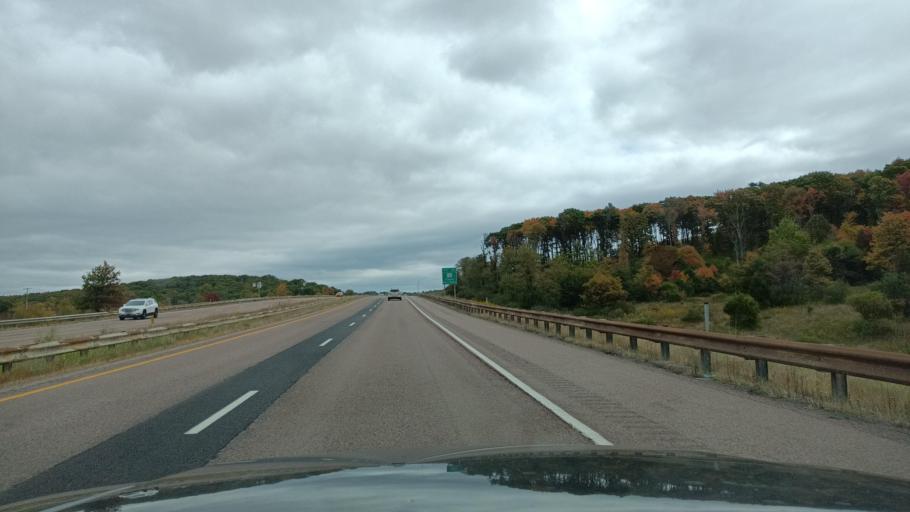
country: US
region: Maryland
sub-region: Allegany County
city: Frostburg
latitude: 39.6867
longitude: -78.9829
